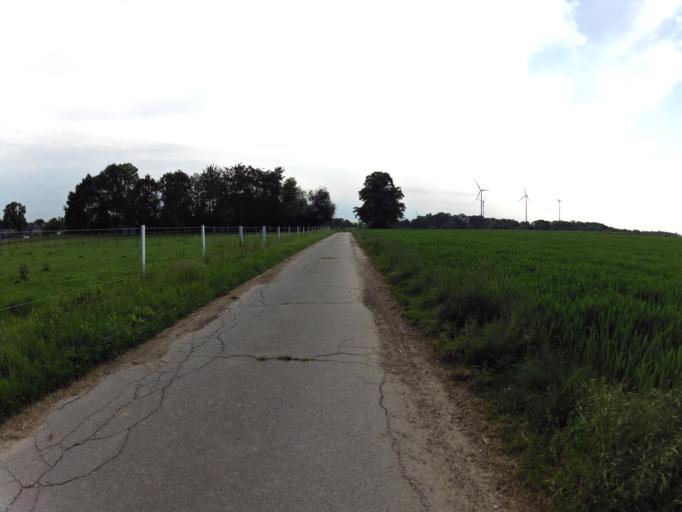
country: DE
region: North Rhine-Westphalia
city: Baesweiler
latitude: 50.9810
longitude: 6.1888
